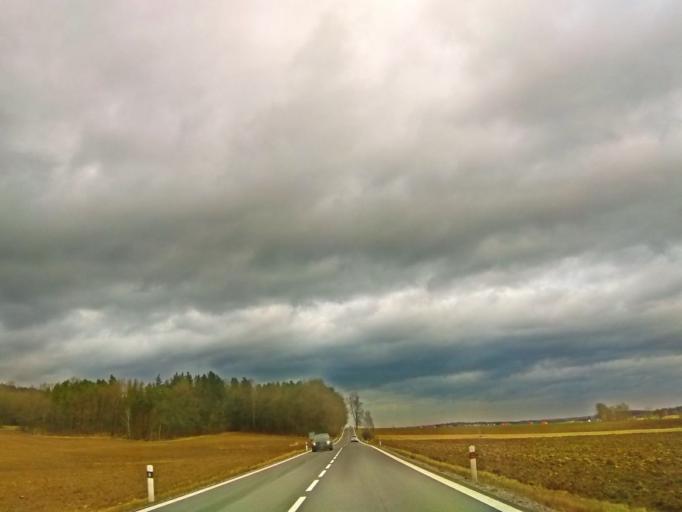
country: CZ
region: Jihocesky
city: Kamenny Ujezd
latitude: 48.8498
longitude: 14.3885
